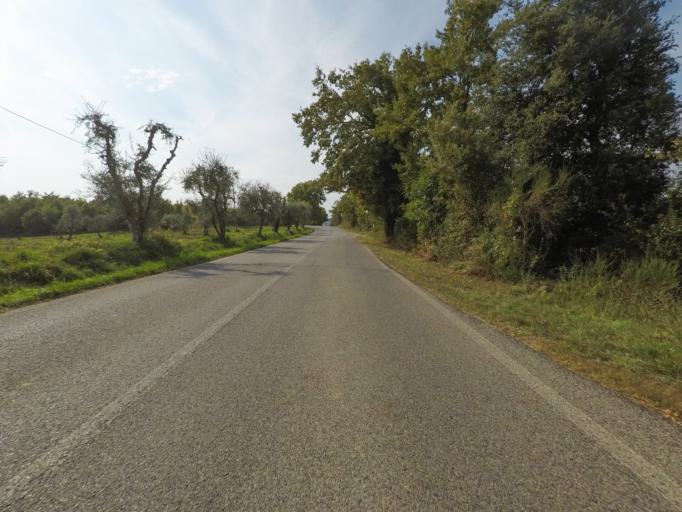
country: IT
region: Tuscany
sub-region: Provincia di Siena
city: Belverde
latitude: 43.3835
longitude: 11.3426
